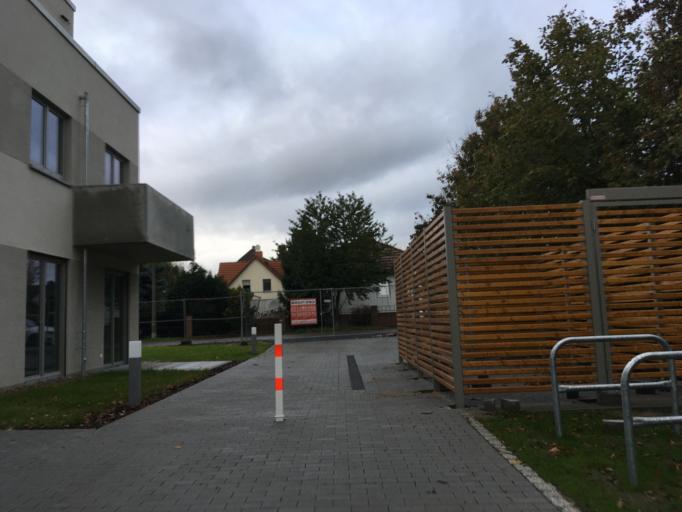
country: DE
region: Berlin
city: Niederschonhausen
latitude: 52.5926
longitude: 13.3925
